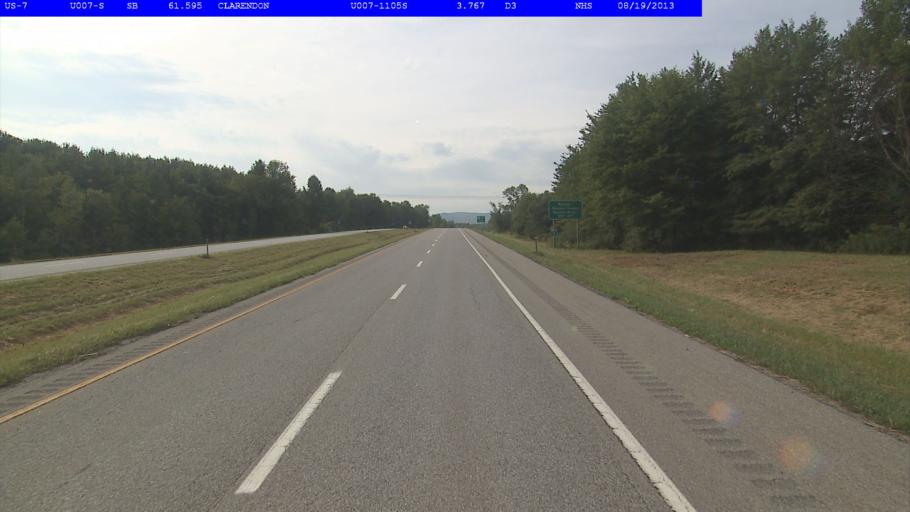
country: US
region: Vermont
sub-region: Rutland County
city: Rutland
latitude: 43.5468
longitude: -72.9608
